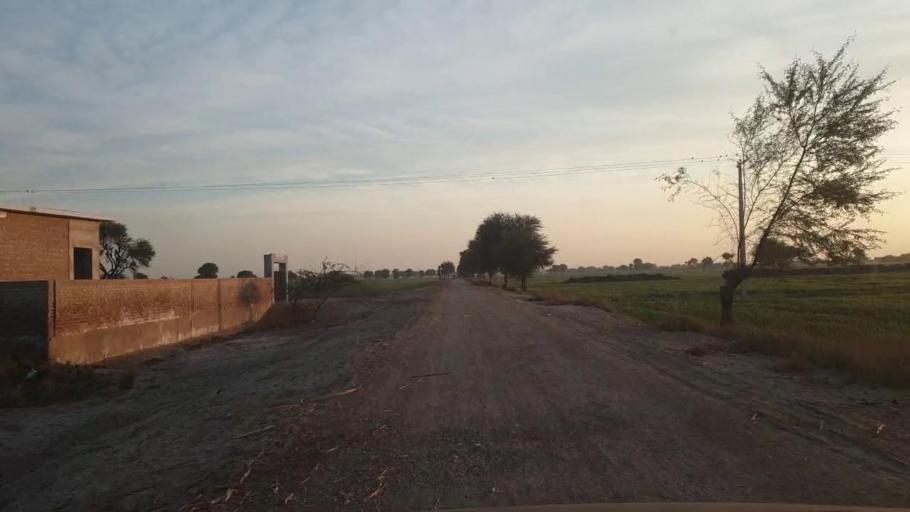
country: PK
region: Sindh
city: Shahpur Chakar
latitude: 26.0525
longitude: 68.5464
